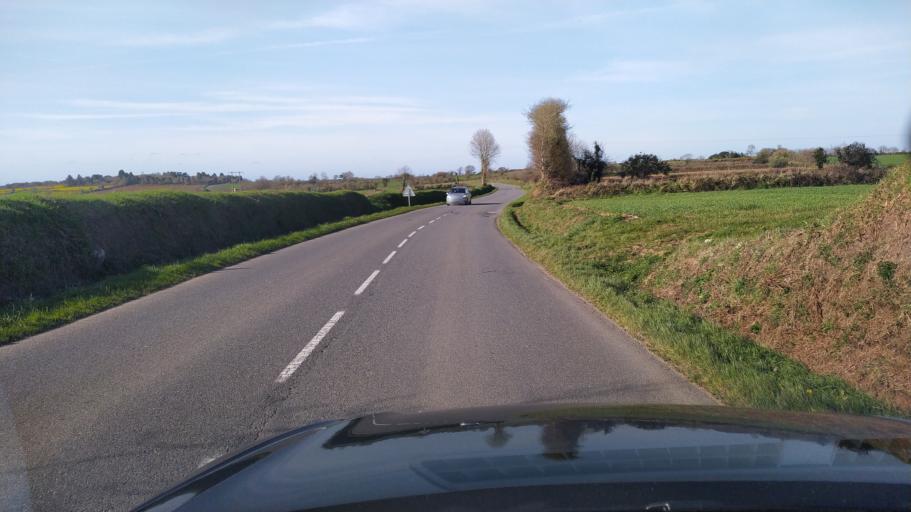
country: FR
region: Brittany
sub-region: Departement du Finistere
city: Lampaul-Guimiliau
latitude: 48.4725
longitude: -4.0218
